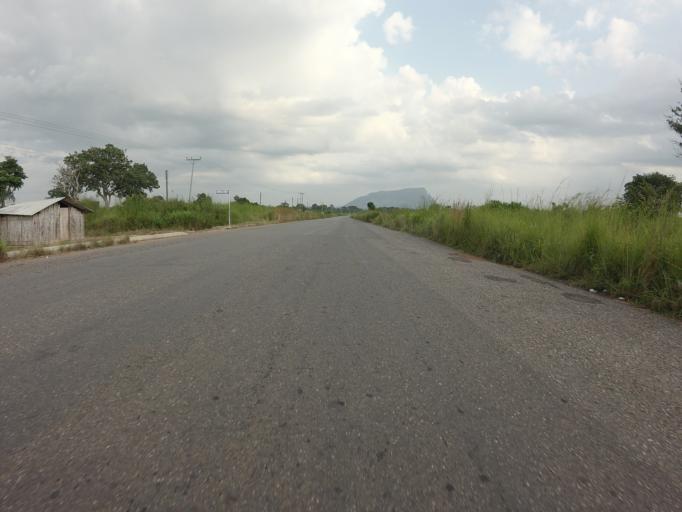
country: GH
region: Volta
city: Ho
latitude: 6.5739
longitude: 0.4842
